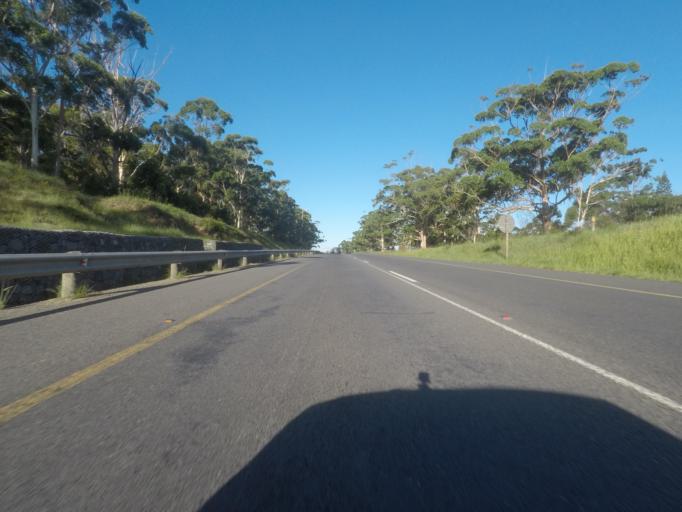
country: ZA
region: Eastern Cape
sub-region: Buffalo City Metropolitan Municipality
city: East London
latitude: -33.0463
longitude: 27.8235
